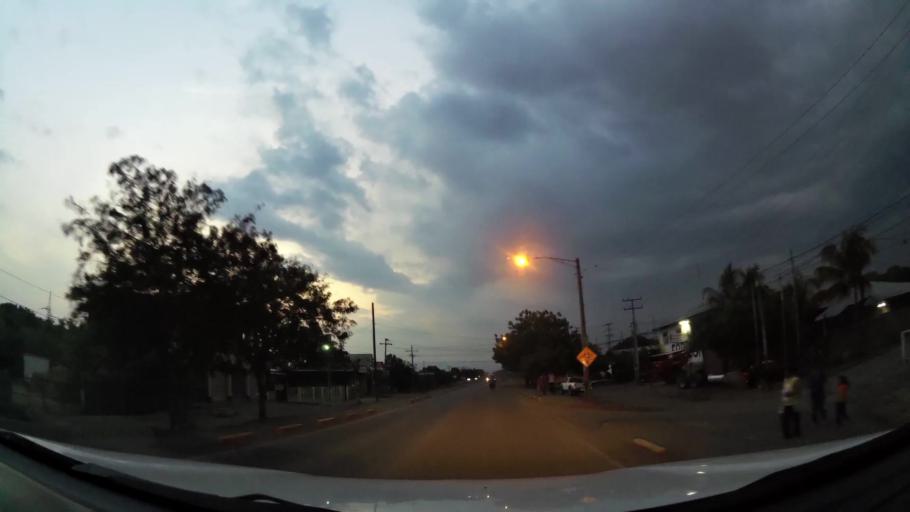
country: NI
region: Matagalpa
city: Ciudad Dario
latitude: 12.8571
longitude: -86.1017
